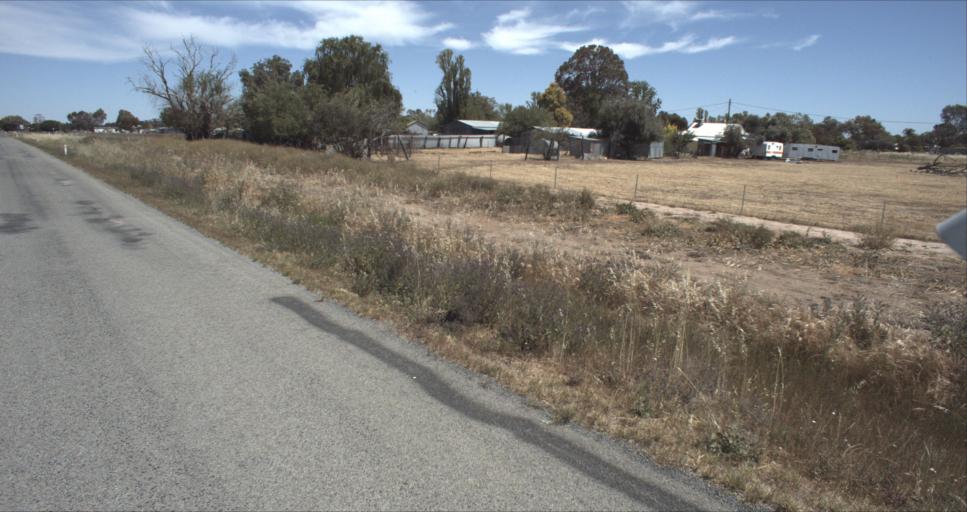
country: AU
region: New South Wales
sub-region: Leeton
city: Leeton
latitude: -34.6007
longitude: 146.4157
